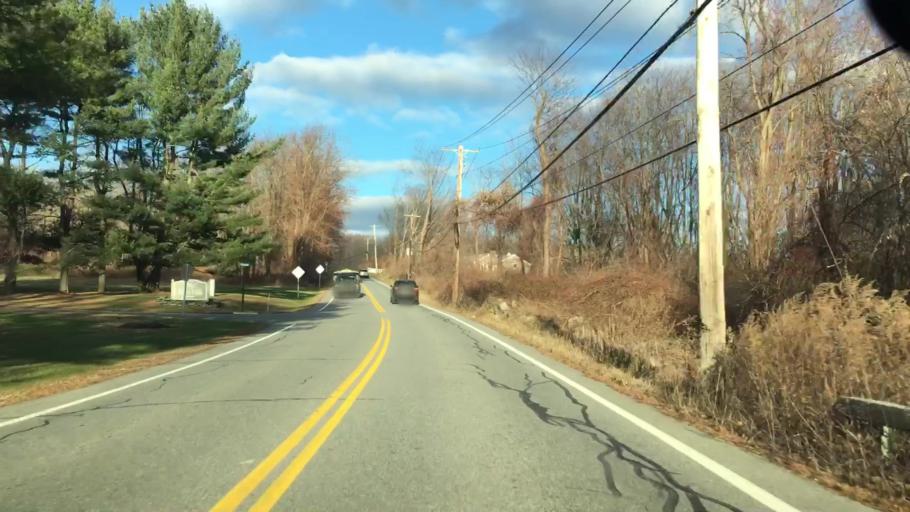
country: US
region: New York
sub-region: Putnam County
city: Lake Carmel
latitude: 41.4430
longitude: -73.6478
